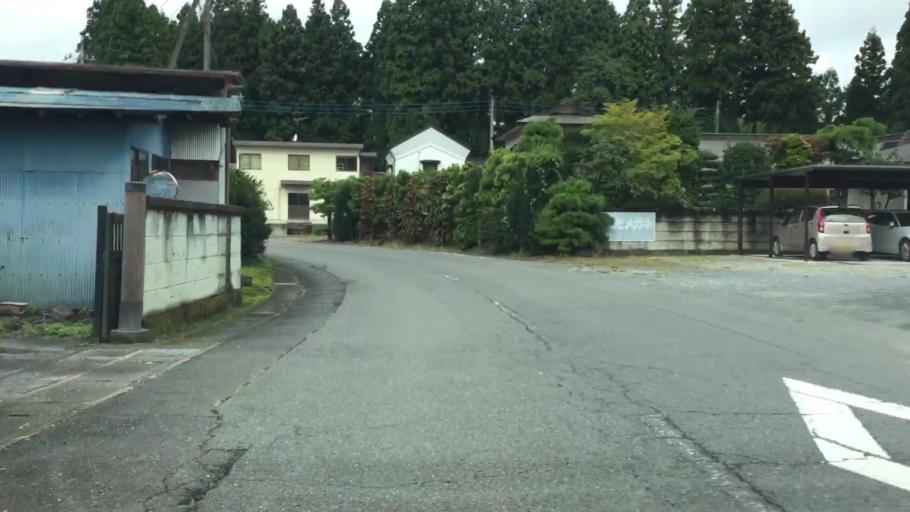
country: JP
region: Tochigi
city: Imaichi
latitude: 36.7595
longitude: 139.6829
